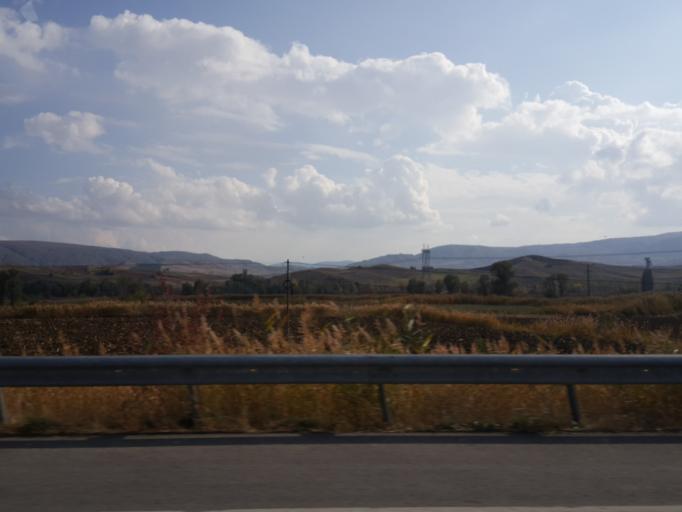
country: TR
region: Corum
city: Seydim
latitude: 40.4260
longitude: 34.7763
